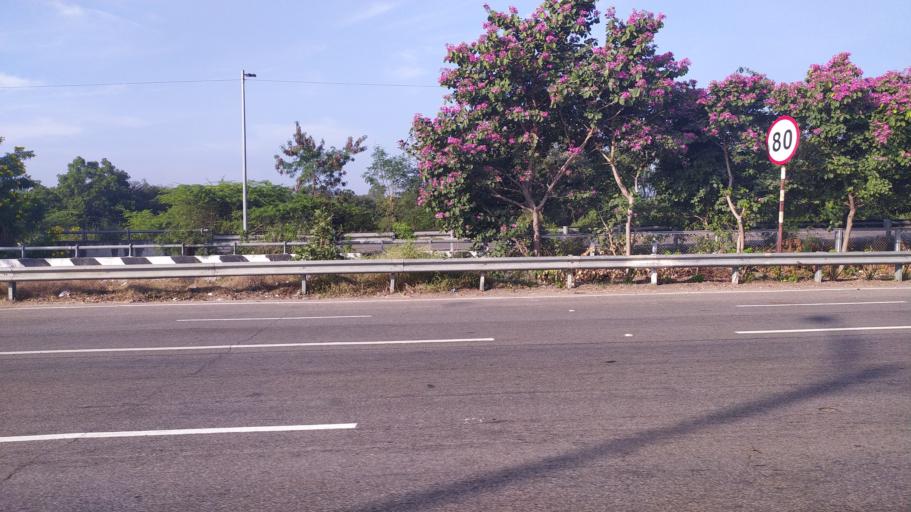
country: IN
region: Telangana
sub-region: Hyderabad
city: Hyderabad
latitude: 17.3555
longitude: 78.3568
